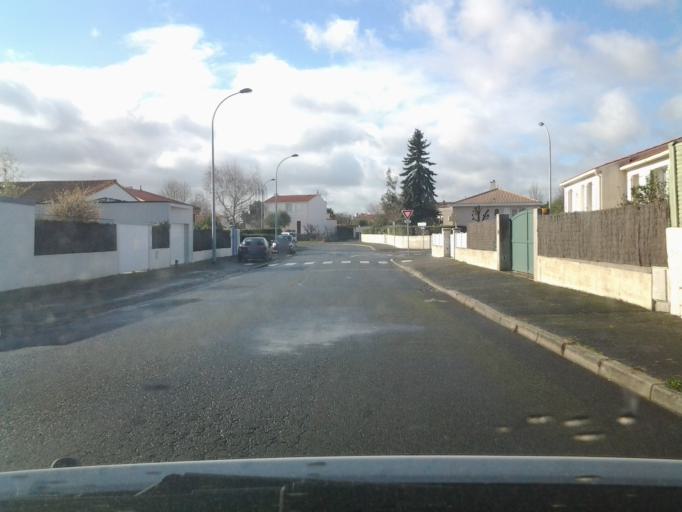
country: FR
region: Pays de la Loire
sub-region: Departement de la Vendee
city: La Roche-sur-Yon
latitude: 46.6627
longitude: -1.4485
